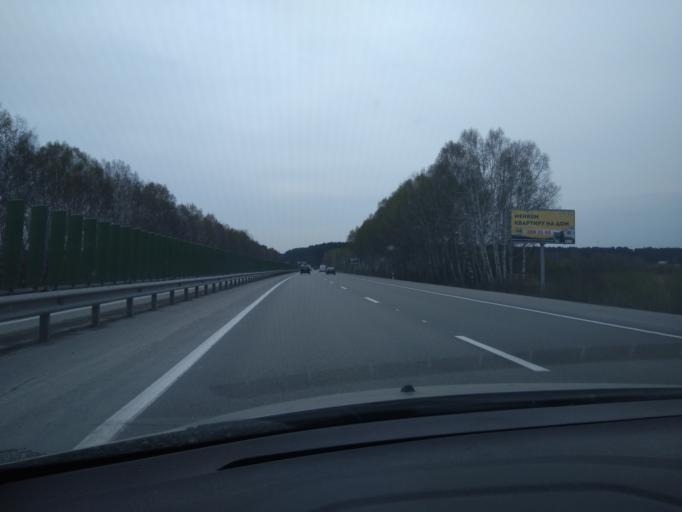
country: RU
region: Sverdlovsk
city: Istok
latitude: 56.7891
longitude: 60.8318
